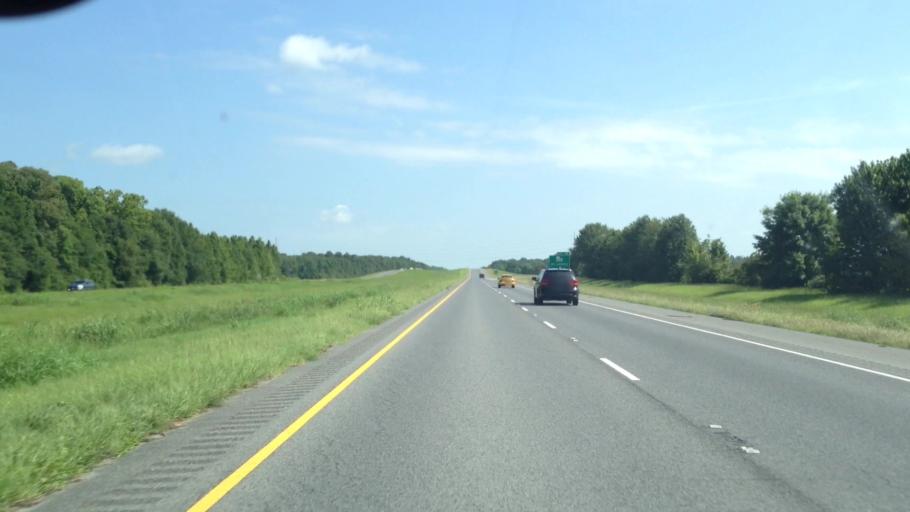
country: US
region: Louisiana
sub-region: Avoyelles Parish
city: Bunkie
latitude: 30.8584
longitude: -92.2281
